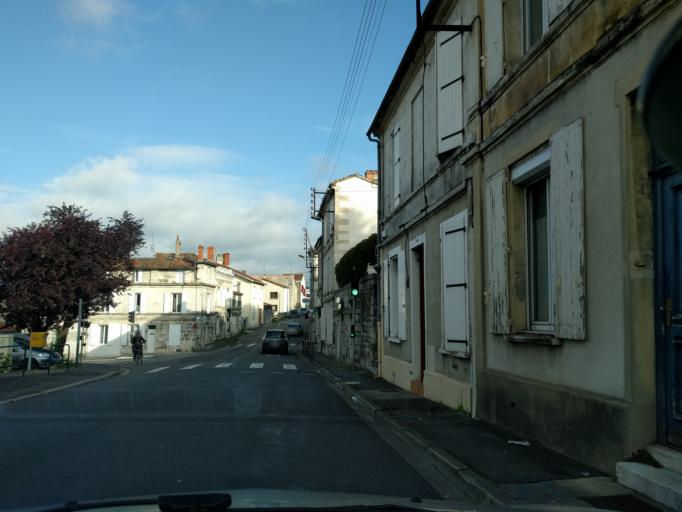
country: FR
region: Poitou-Charentes
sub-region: Departement de la Charente
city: Angouleme
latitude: 45.6457
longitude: 0.1526
